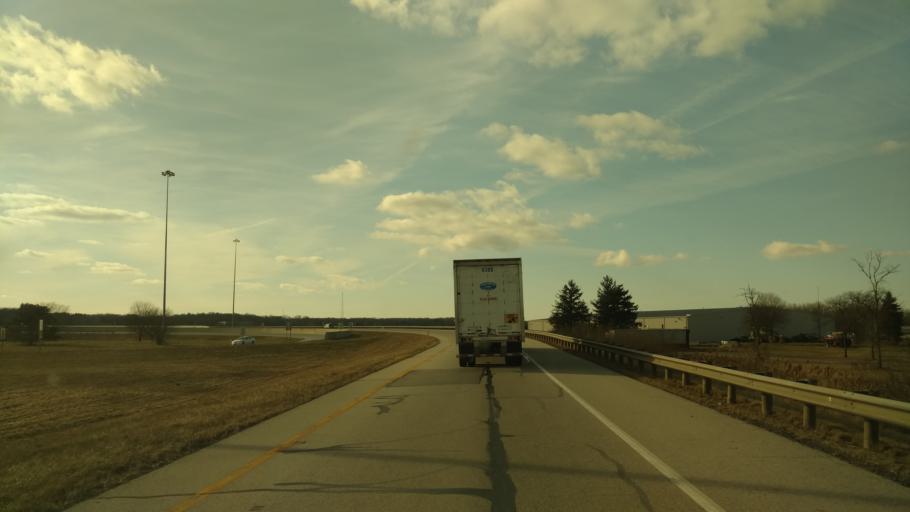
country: US
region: Ohio
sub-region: Medina County
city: Westfield Center
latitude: 41.0316
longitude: -81.8961
